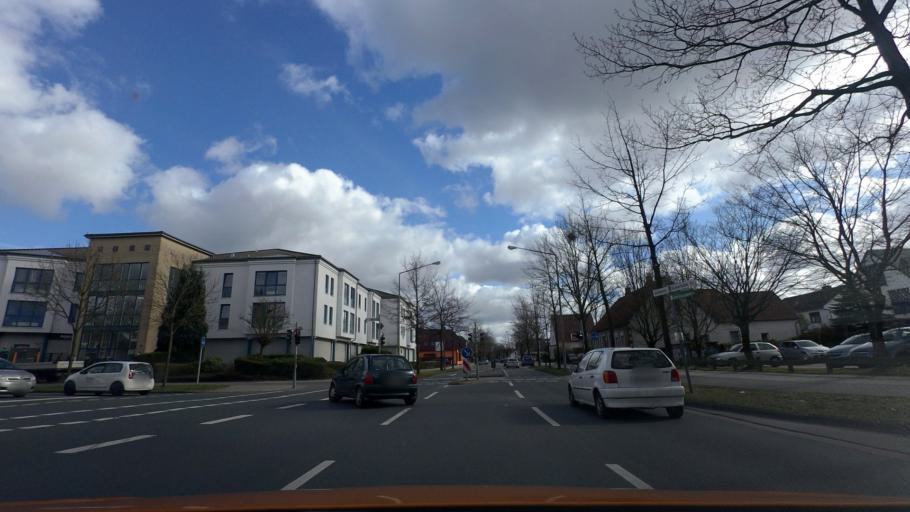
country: DE
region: Lower Saxony
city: Oldenburg
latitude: 53.1408
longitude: 8.1767
